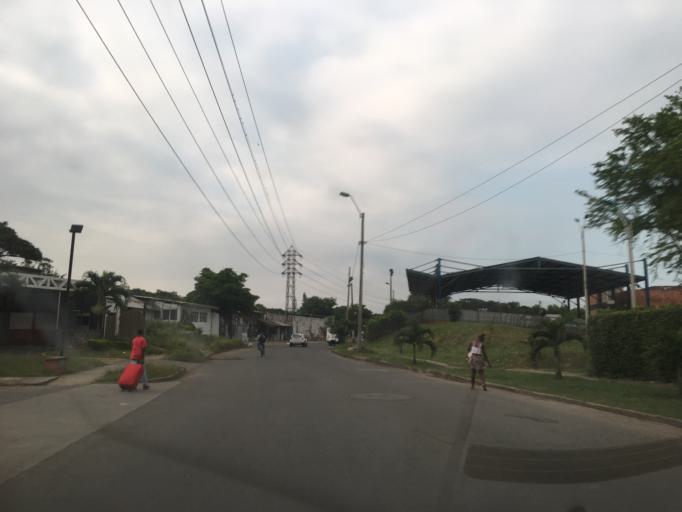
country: CO
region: Valle del Cauca
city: Cali
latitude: 3.4047
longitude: -76.5234
